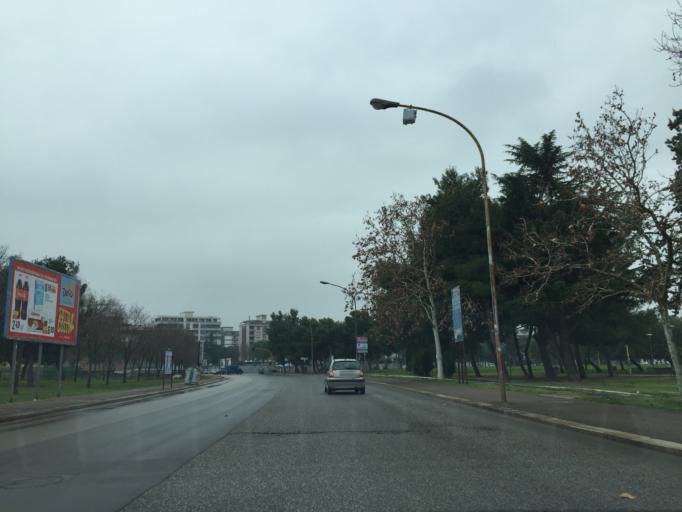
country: IT
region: Apulia
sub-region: Provincia di Foggia
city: Foggia
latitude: 41.4634
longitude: 15.5329
